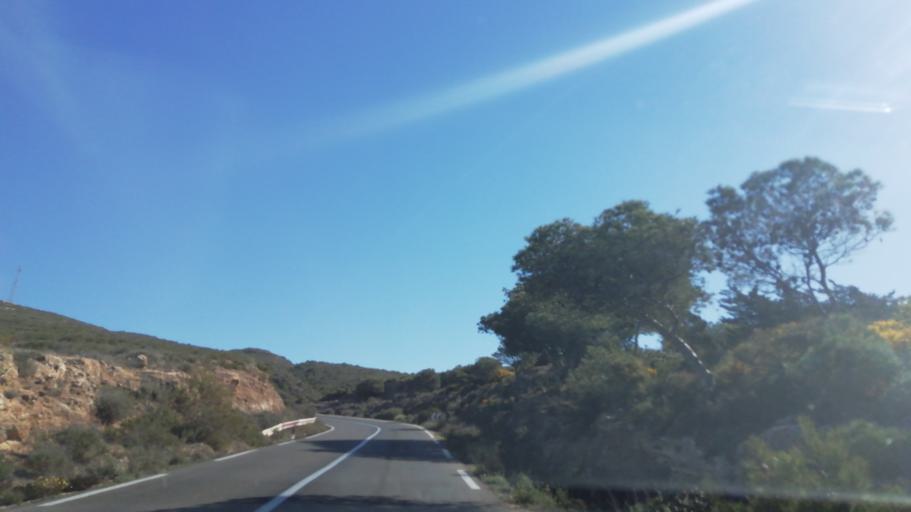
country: DZ
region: Ain Temouchent
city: El Amria
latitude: 35.6480
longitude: -1.0423
